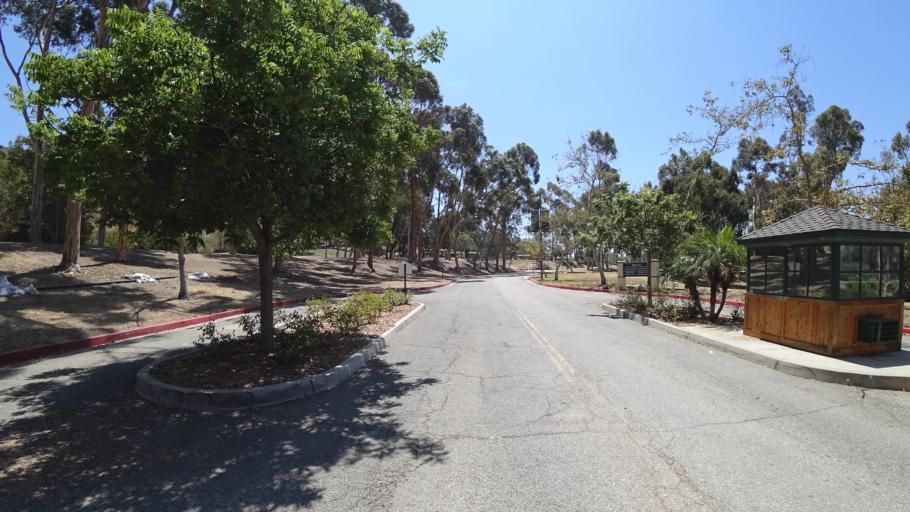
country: US
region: California
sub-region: Los Angeles County
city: Ladera Heights
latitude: 34.0114
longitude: -118.3704
